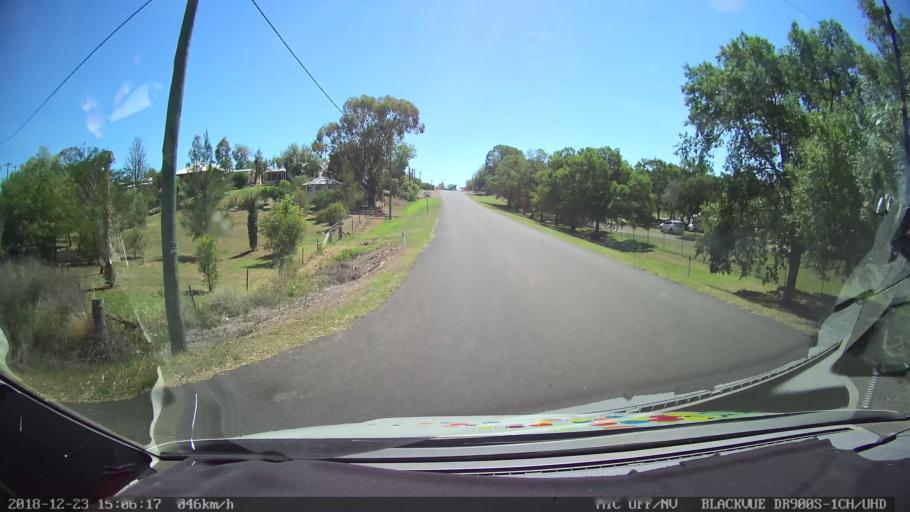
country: AU
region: New South Wales
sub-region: Tamworth Municipality
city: Manilla
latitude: -30.7451
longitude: 150.7299
